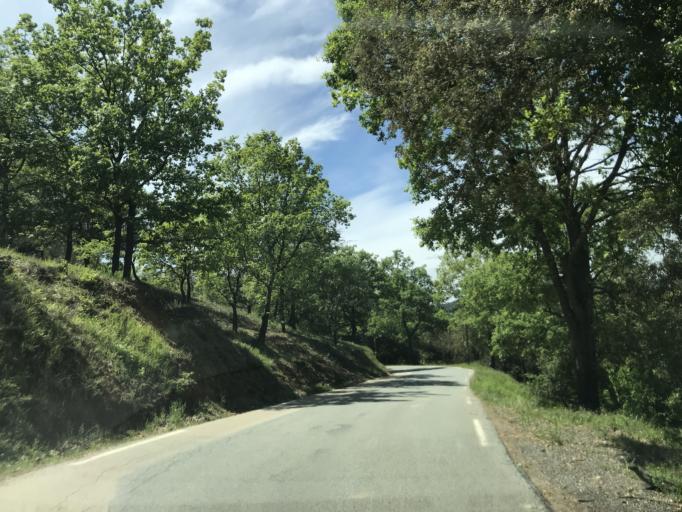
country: FR
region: Provence-Alpes-Cote d'Azur
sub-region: Departement du Var
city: Tanneron
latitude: 43.5860
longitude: 6.8199
